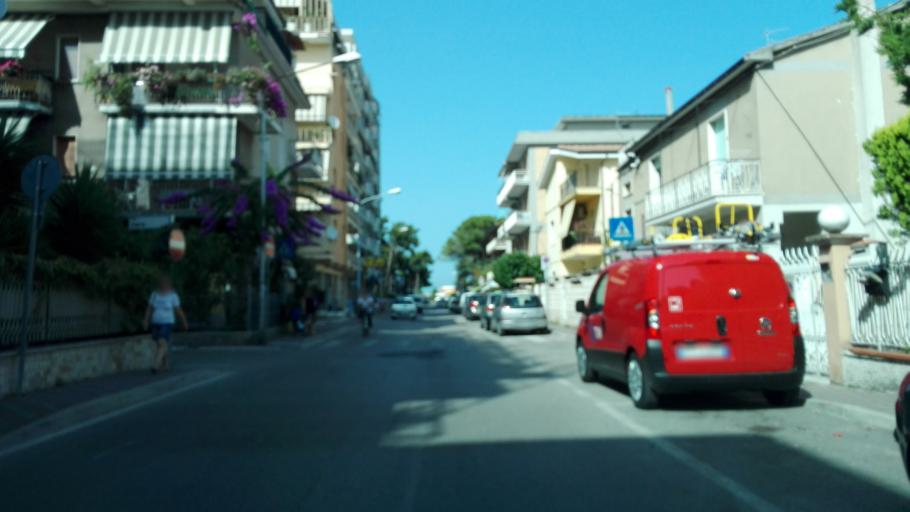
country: IT
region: Abruzzo
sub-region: Provincia di Pescara
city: Montesilvano Marina
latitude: 42.4987
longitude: 14.1769
